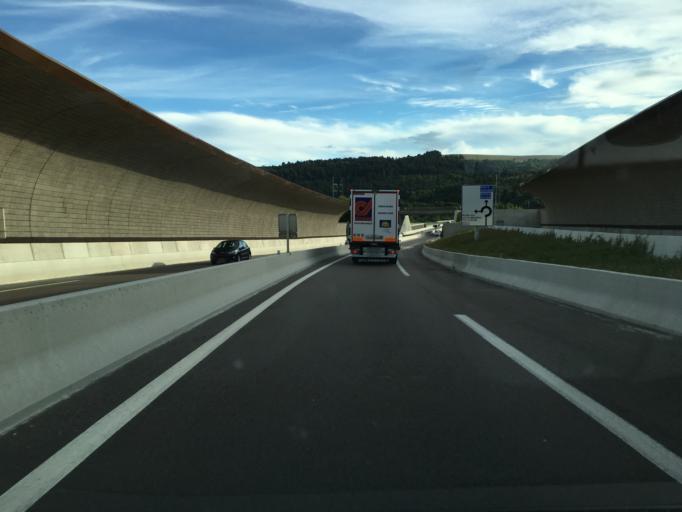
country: FR
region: Bourgogne
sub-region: Departement de la Cote-d'Or
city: Plombieres-les-Dijon
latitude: 47.3377
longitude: 4.9856
